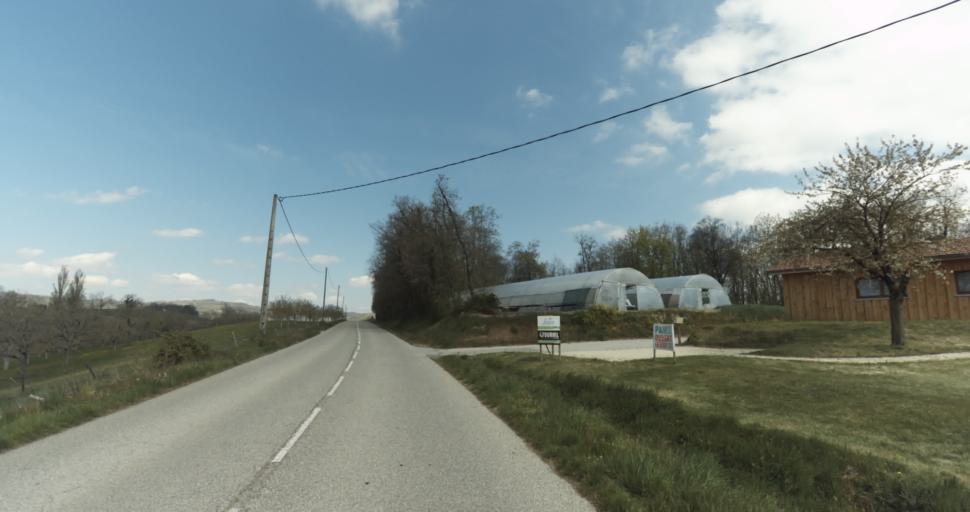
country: FR
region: Rhone-Alpes
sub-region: Departement de l'Isere
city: Saint-Verand
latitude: 45.1784
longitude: 5.3172
